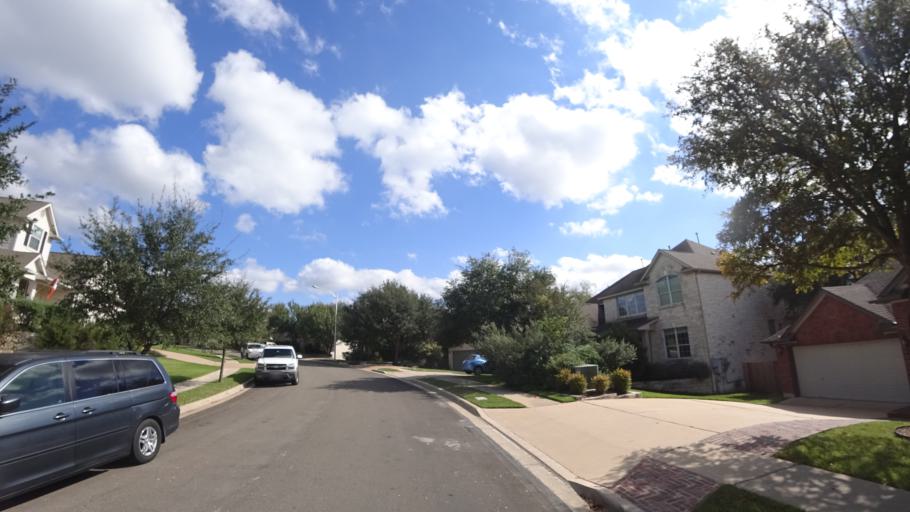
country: US
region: Texas
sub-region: Travis County
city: Barton Creek
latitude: 30.2534
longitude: -97.8848
